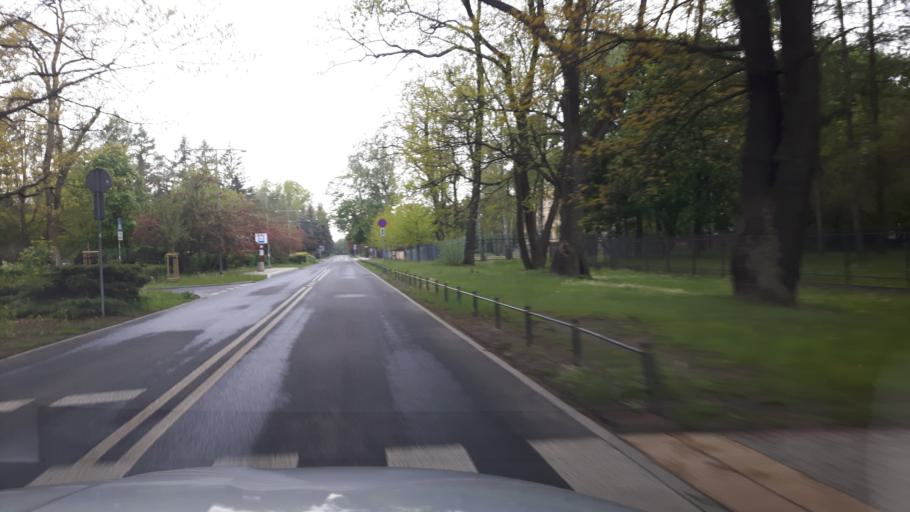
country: PL
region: Masovian Voivodeship
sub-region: Warszawa
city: Rembertow
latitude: 52.2681
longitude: 21.1773
